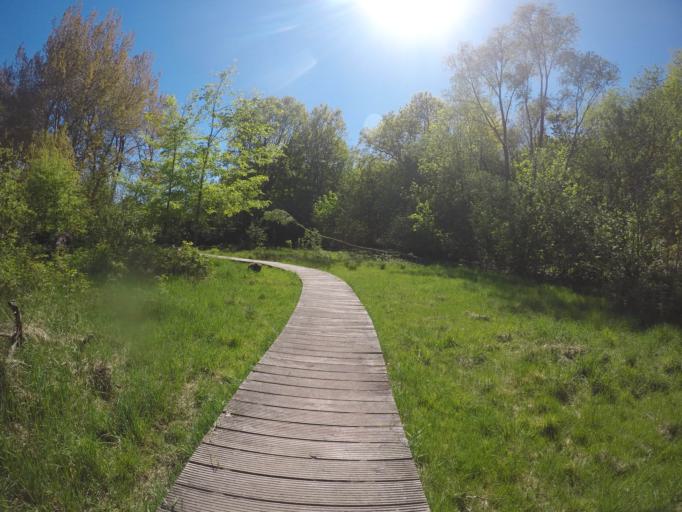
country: DE
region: Hamburg
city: Sasel
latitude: 53.6296
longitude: 10.1124
